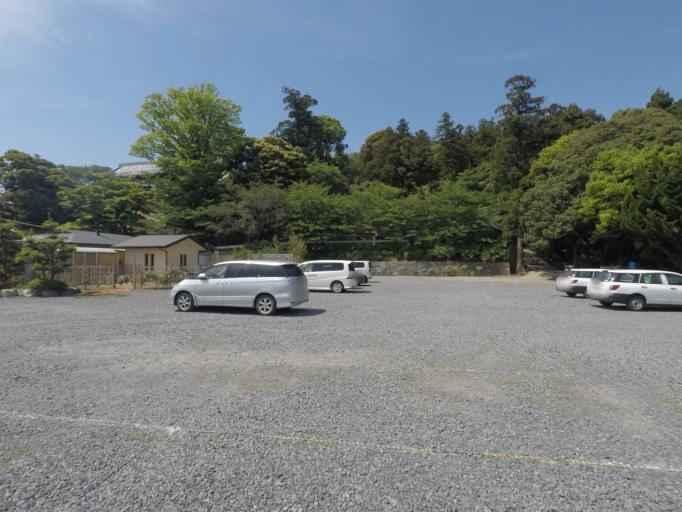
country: JP
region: Ibaraki
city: Iwase
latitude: 36.3301
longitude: 140.1215
